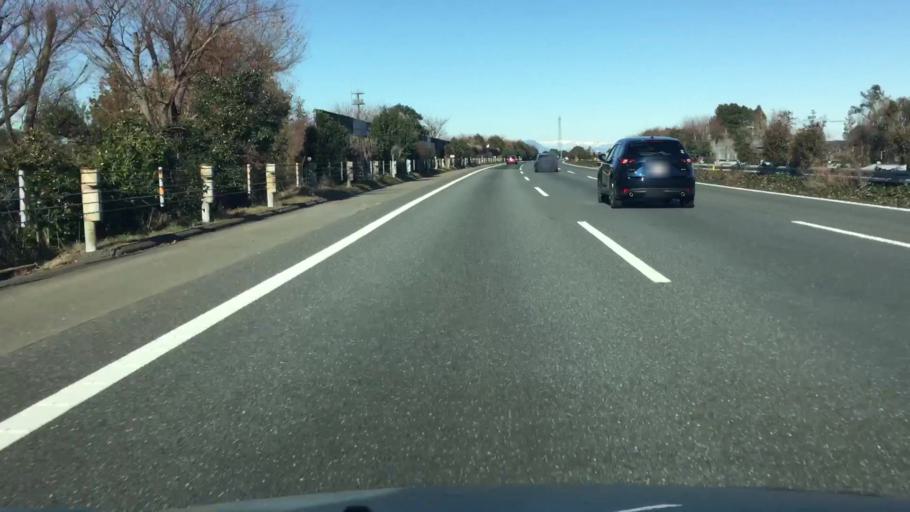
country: JP
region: Saitama
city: Yorii
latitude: 36.1375
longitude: 139.2279
